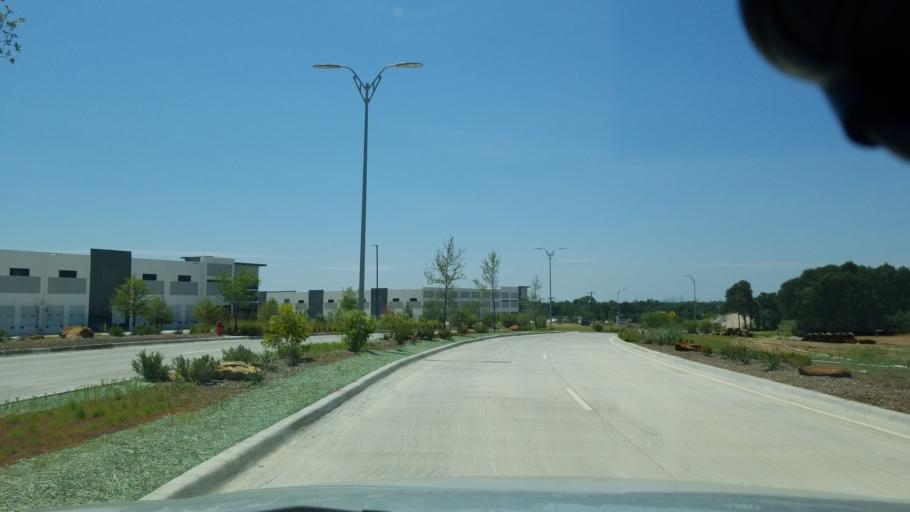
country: US
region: Texas
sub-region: Tarrant County
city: Euless
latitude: 32.8409
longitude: -97.0306
